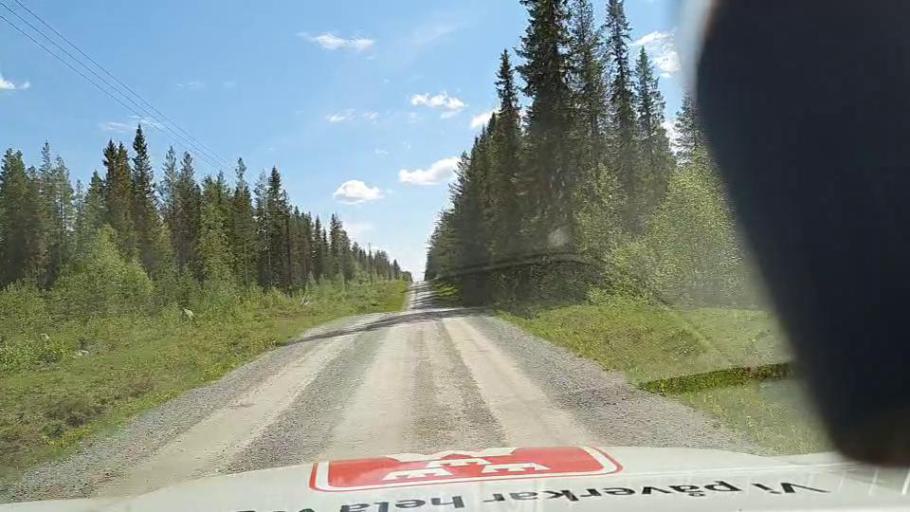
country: SE
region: Jaemtland
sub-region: Stroemsunds Kommun
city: Stroemsund
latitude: 64.4833
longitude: 15.5920
